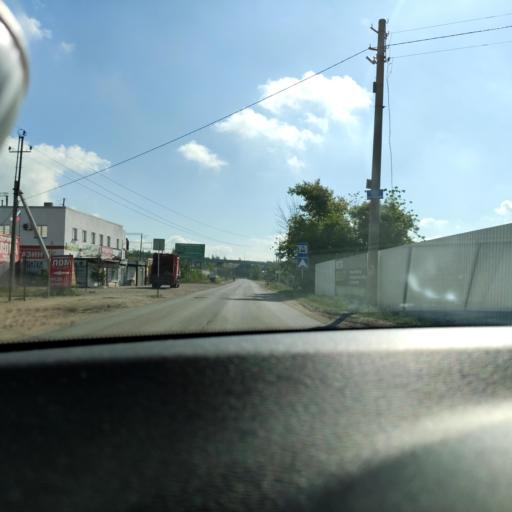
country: RU
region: Samara
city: Volzhskiy
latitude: 53.4336
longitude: 50.1091
